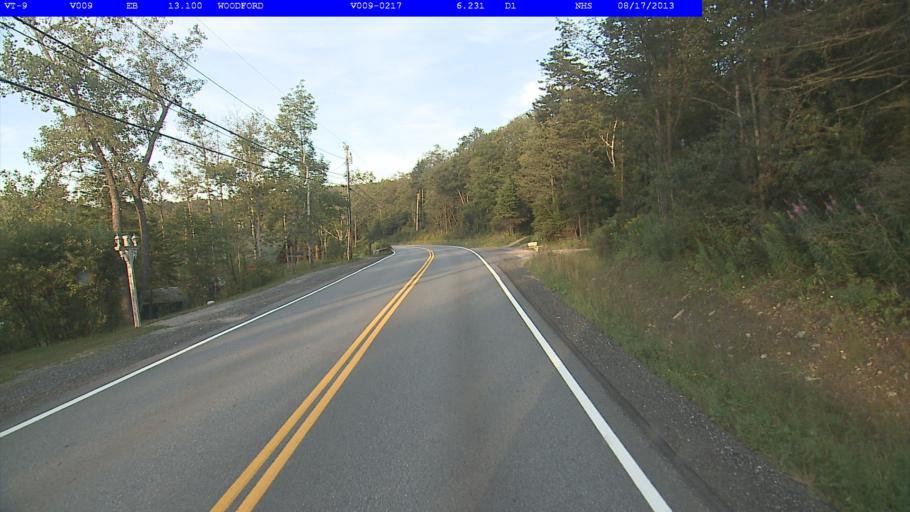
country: US
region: Vermont
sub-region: Bennington County
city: Bennington
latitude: 42.8895
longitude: -73.0681
